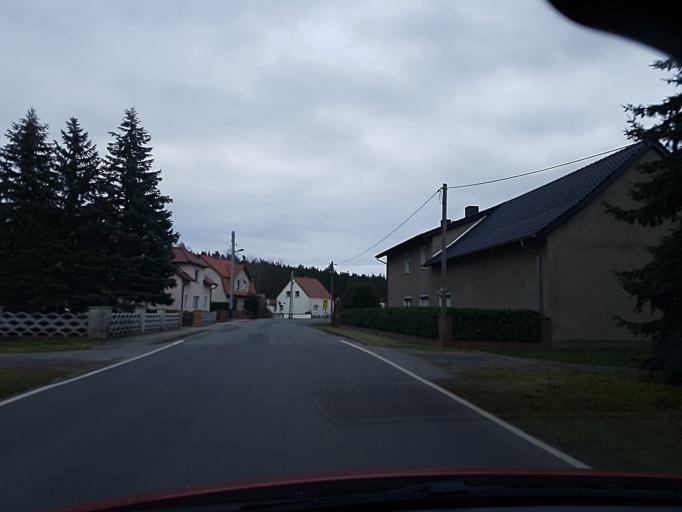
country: DE
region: Brandenburg
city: Bad Liebenwerda
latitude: 51.5537
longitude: 13.4233
